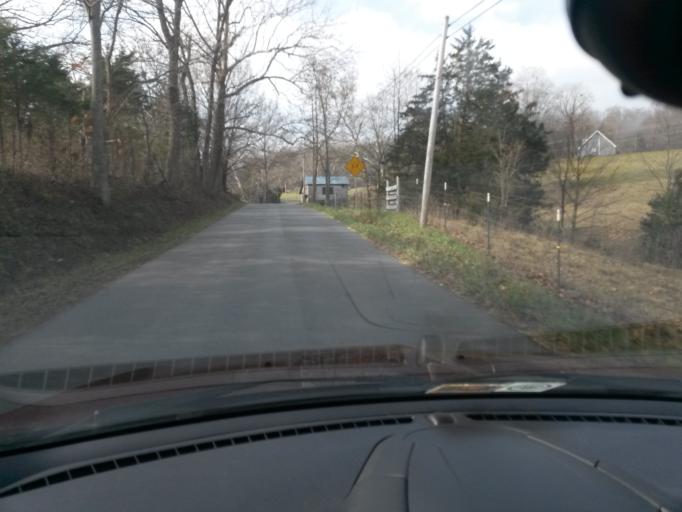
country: US
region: Virginia
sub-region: Botetourt County
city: Fincastle
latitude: 37.5838
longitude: -79.8713
